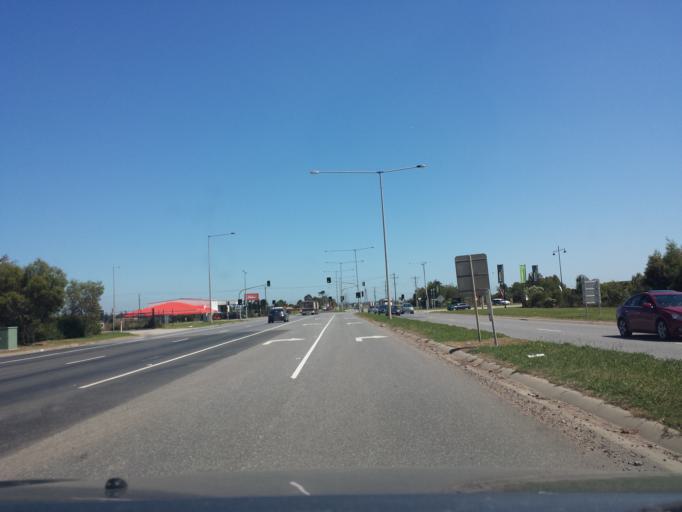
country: AU
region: Victoria
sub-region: Cardinia
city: Pakenham South
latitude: -38.0969
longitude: 145.4891
